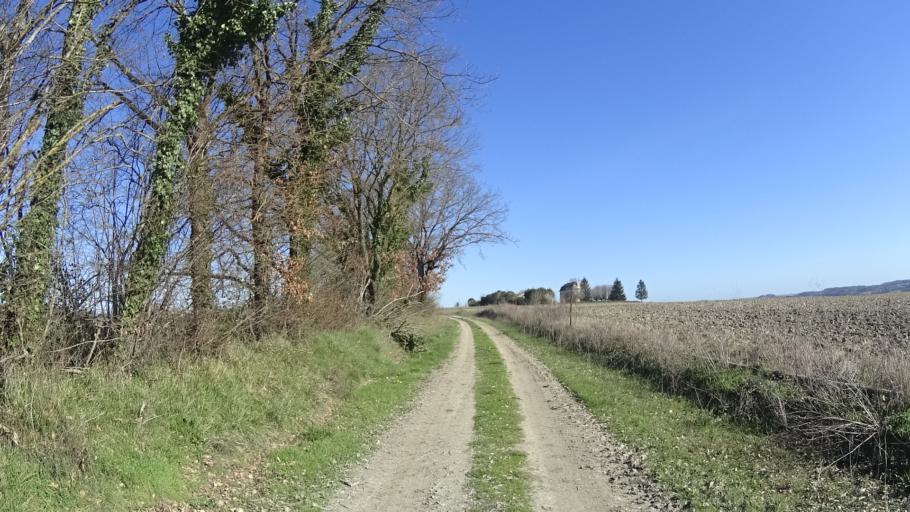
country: FR
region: Aquitaine
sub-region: Departement de la Dordogne
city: Saint-Aulaye
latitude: 45.2363
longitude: 0.1331
